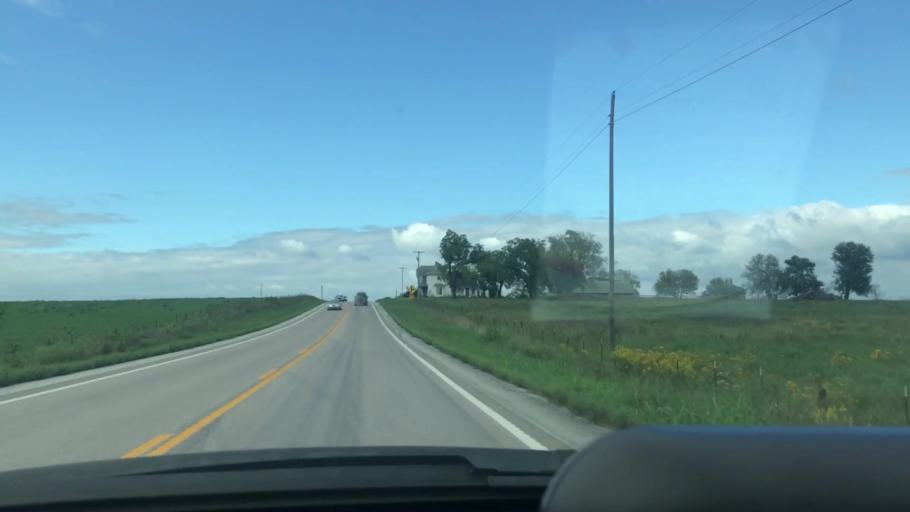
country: US
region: Missouri
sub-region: Hickory County
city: Hermitage
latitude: 37.9527
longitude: -93.2074
